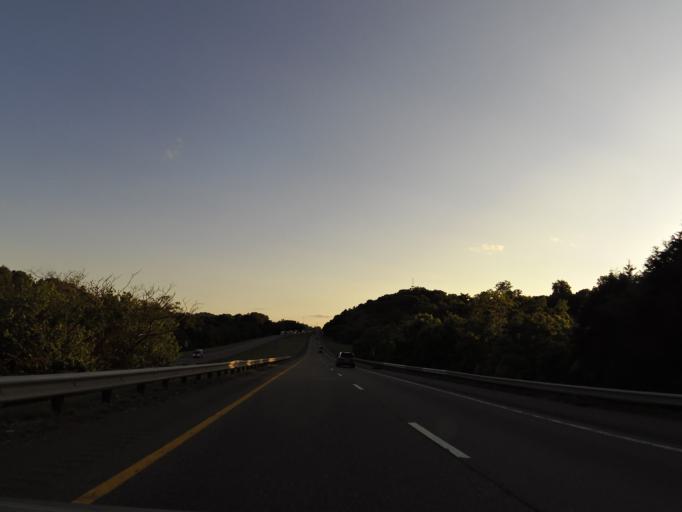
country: US
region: Tennessee
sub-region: Sullivan County
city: Colonial Heights
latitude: 36.4834
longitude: -82.4779
